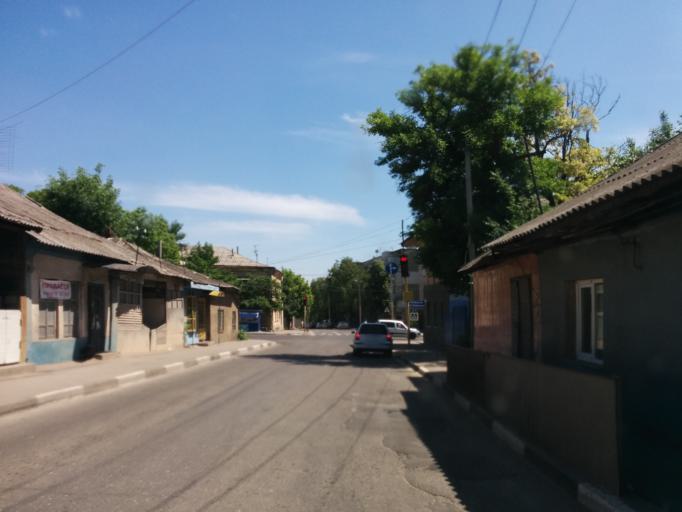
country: MD
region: Raionul Soroca
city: Soroca
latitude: 48.1621
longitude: 28.3007
